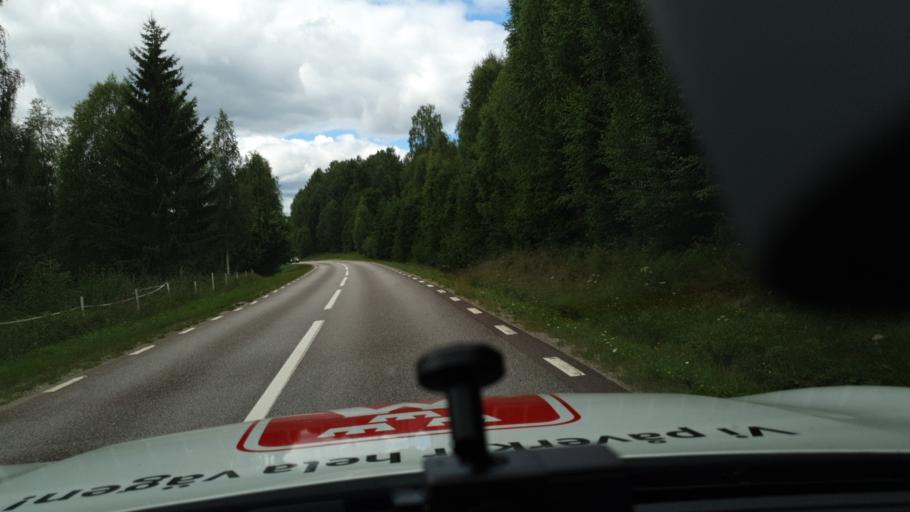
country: NO
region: Hedmark
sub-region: Trysil
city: Innbygda
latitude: 60.8842
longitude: 12.6516
